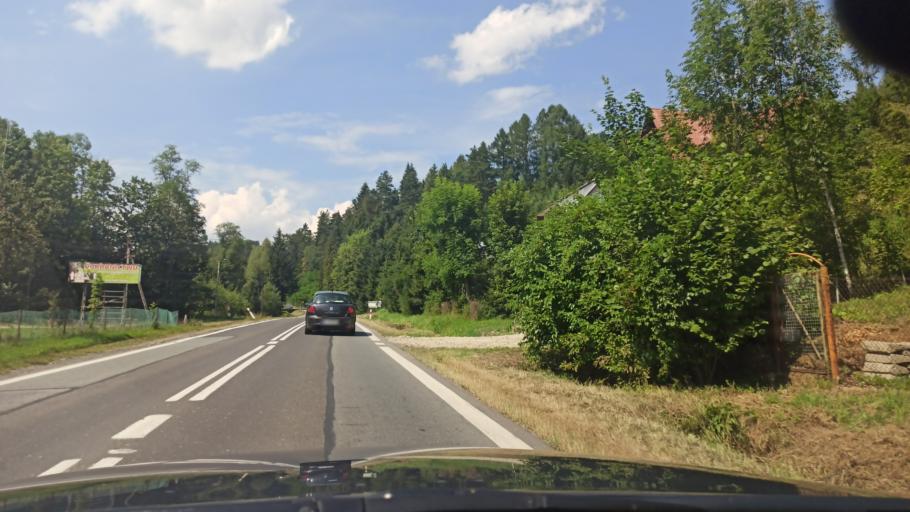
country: PL
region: Lesser Poland Voivodeship
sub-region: Powiat nowotarski
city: Krosnica
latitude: 49.4393
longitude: 20.3582
